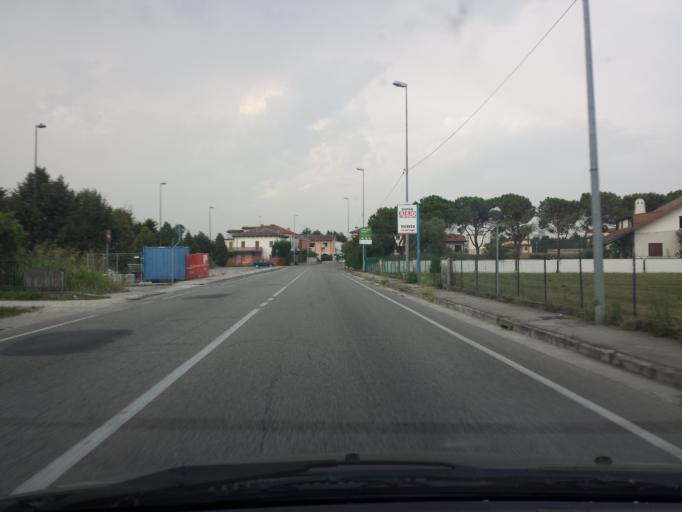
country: IT
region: Veneto
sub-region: Provincia di Vicenza
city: Vicenza
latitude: 45.5740
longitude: 11.5503
